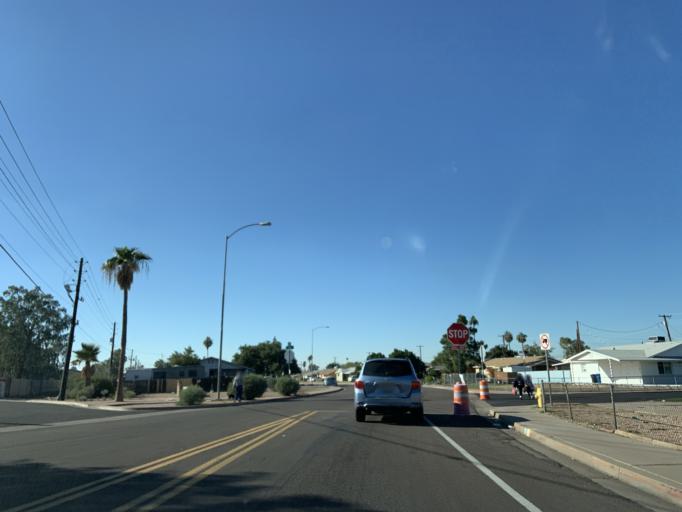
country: US
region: Arizona
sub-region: Maricopa County
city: Mesa
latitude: 33.4004
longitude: -111.8586
